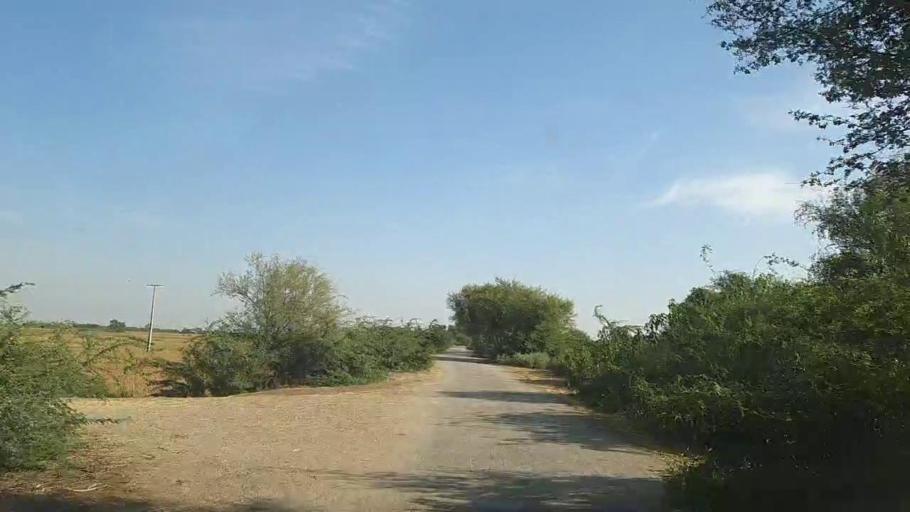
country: PK
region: Sindh
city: Bulri
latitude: 24.7958
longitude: 68.3399
